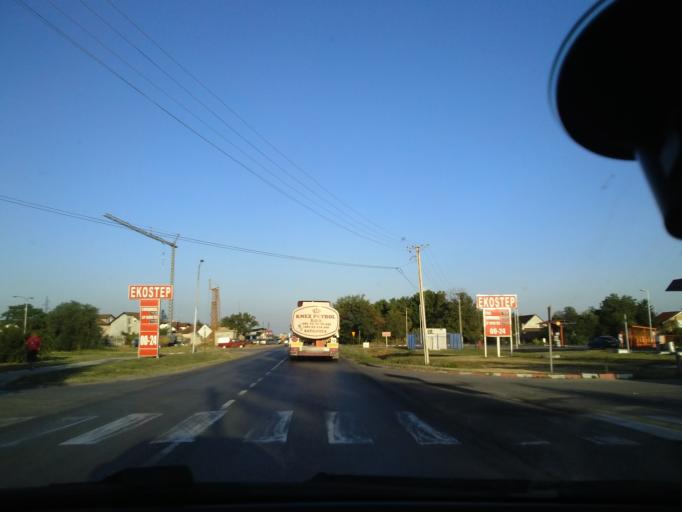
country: RS
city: Rumenka
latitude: 45.2900
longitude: 19.7492
